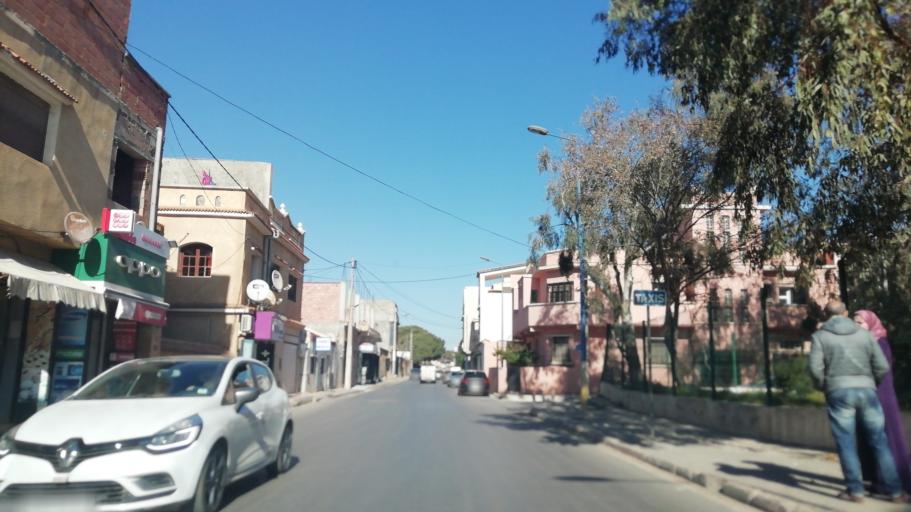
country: DZ
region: Oran
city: Bir el Djir
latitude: 35.7506
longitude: -0.5661
